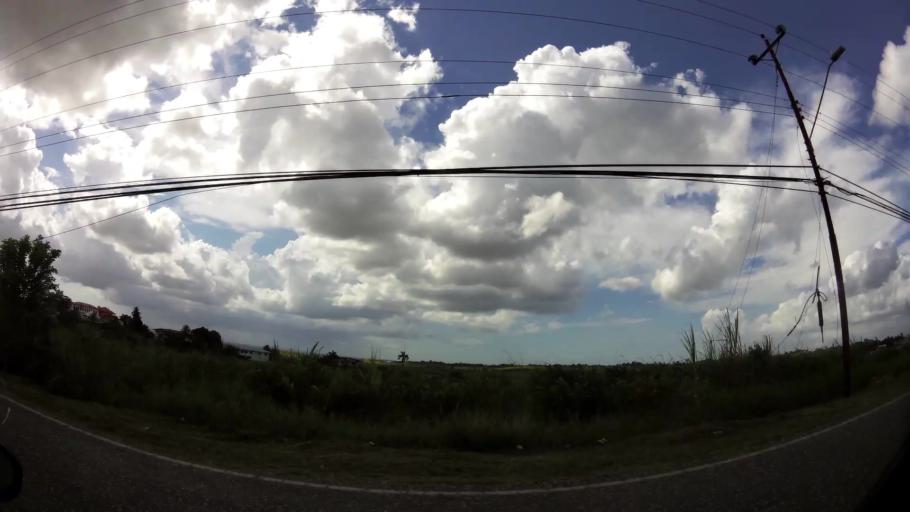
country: TT
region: Penal/Debe
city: Debe
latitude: 10.2262
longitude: -61.4422
